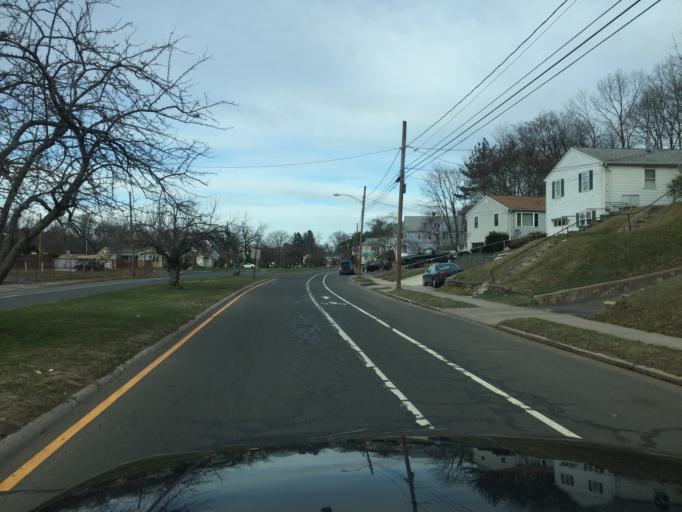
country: US
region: Connecticut
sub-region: Hartford County
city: New Britain
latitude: 41.6836
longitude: -72.7869
